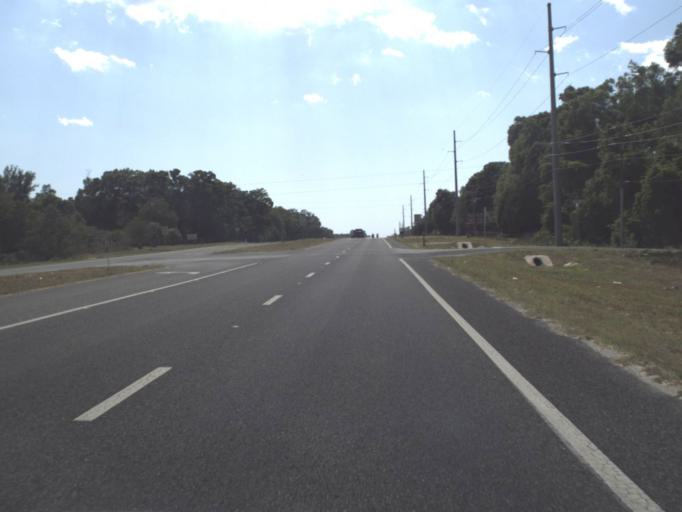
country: US
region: Florida
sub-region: Marion County
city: Ocala
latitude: 29.1866
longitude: -82.2406
